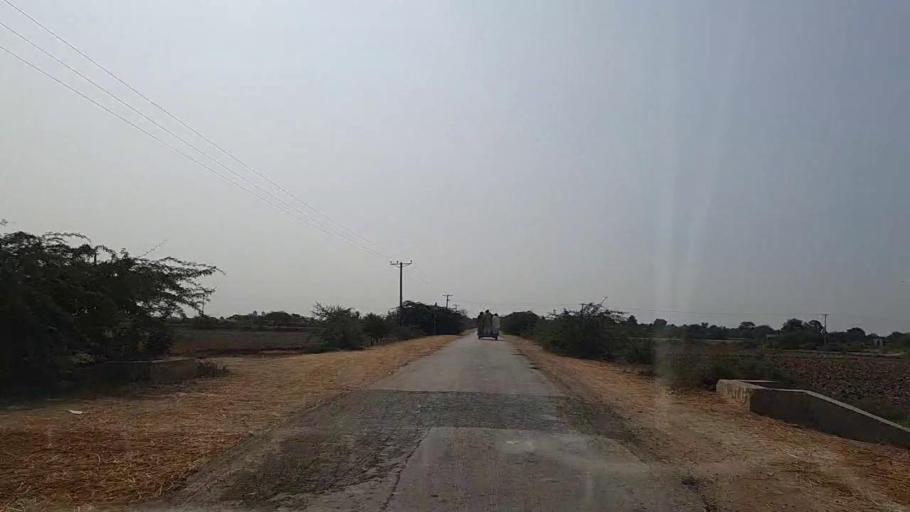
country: PK
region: Sindh
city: Chuhar Jamali
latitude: 24.3745
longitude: 67.9683
